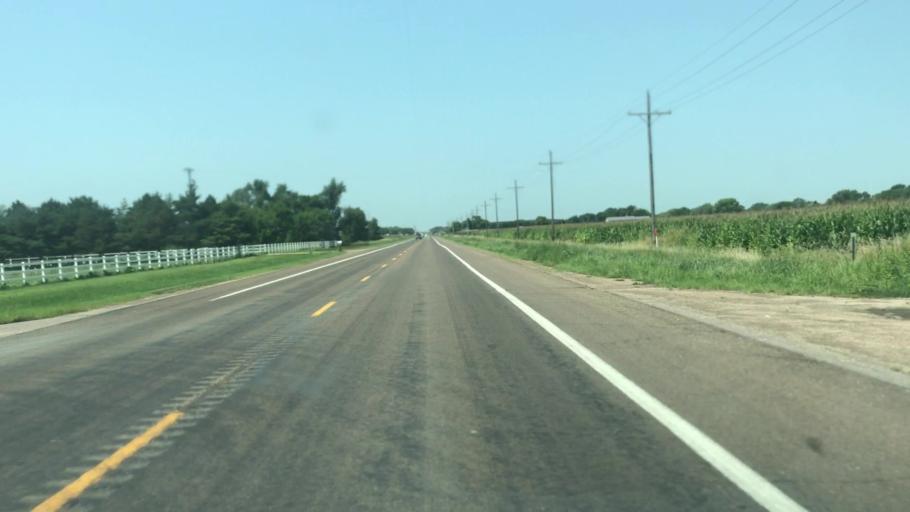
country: US
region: Nebraska
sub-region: Hall County
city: Grand Island
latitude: 40.8869
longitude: -98.3255
